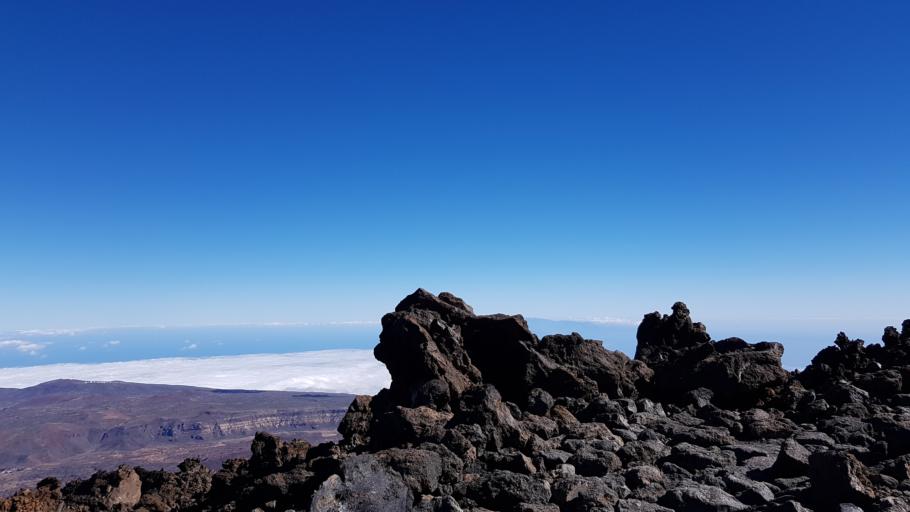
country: ES
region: Canary Islands
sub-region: Provincia de Santa Cruz de Tenerife
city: La Guancha
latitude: 28.2724
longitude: -16.6387
